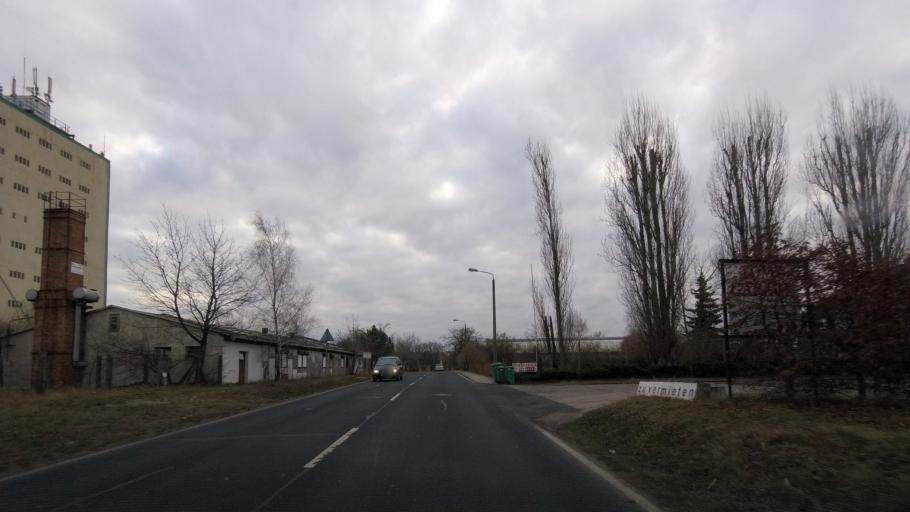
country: DE
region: Brandenburg
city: Juterbog
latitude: 52.0062
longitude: 13.0738
